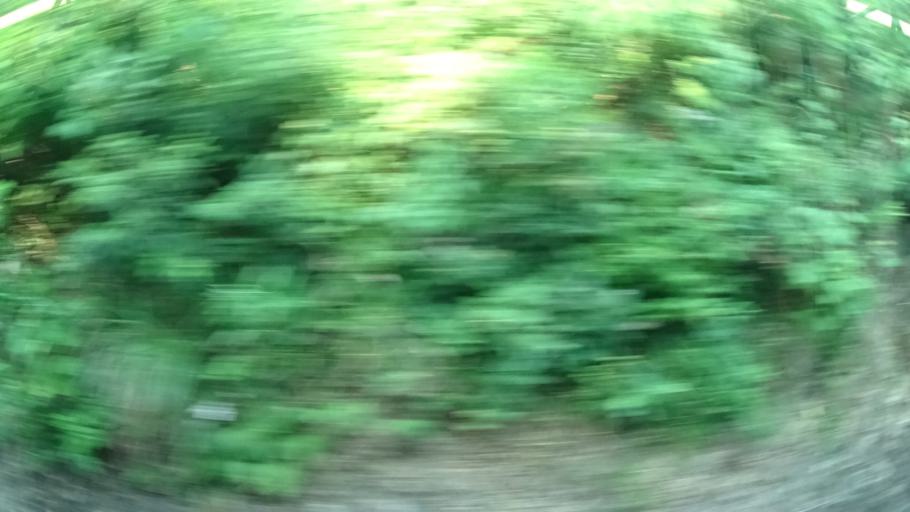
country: JP
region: Ibaraki
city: Takahagi
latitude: 36.6667
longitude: 140.6834
